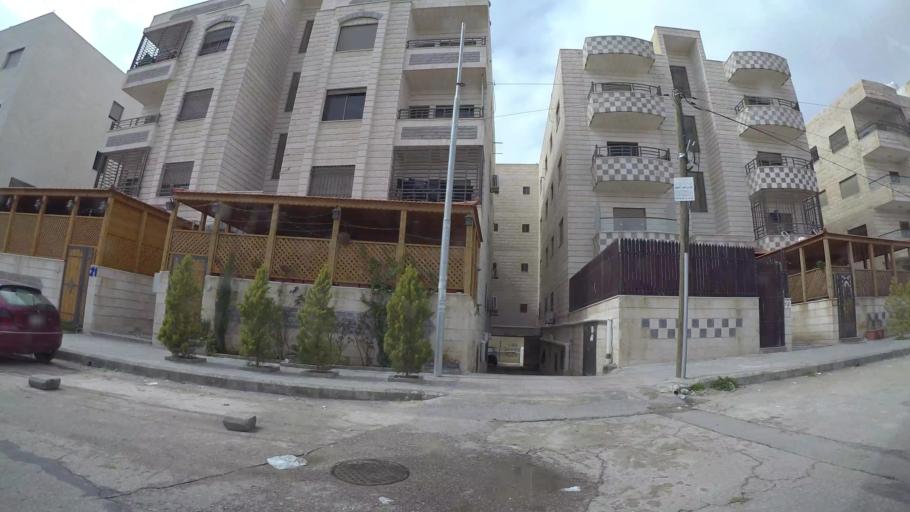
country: JO
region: Amman
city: Amman
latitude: 31.9902
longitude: 35.9234
